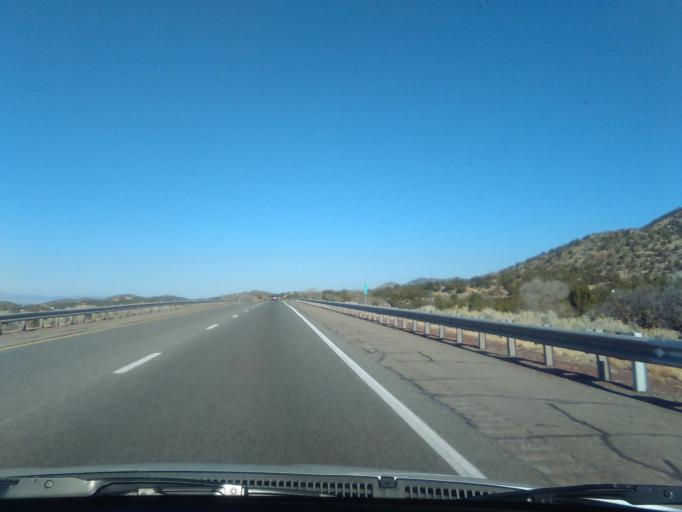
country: US
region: New Mexico
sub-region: Santa Fe County
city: Eldorado at Santa Fe
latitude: 35.5838
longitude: -105.9001
